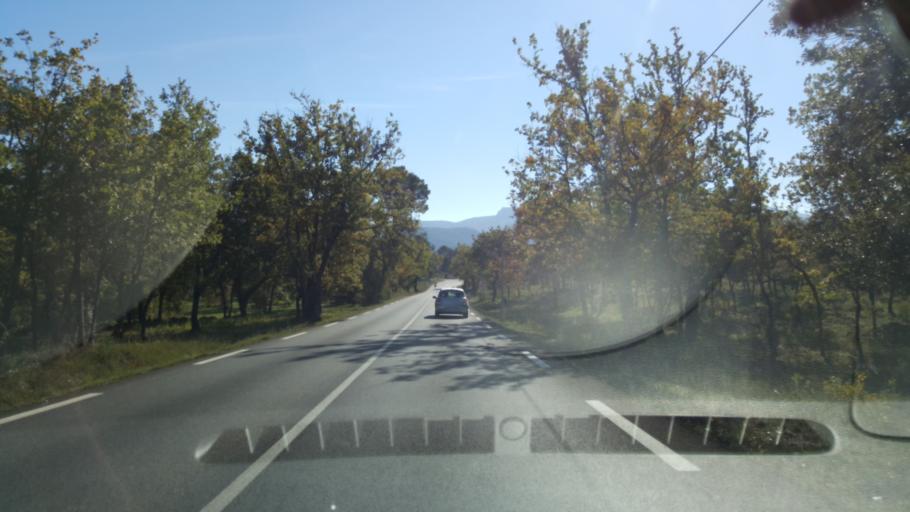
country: FR
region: Provence-Alpes-Cote d'Azur
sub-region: Departement du Var
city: Rougiers
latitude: 43.4113
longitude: 5.8252
